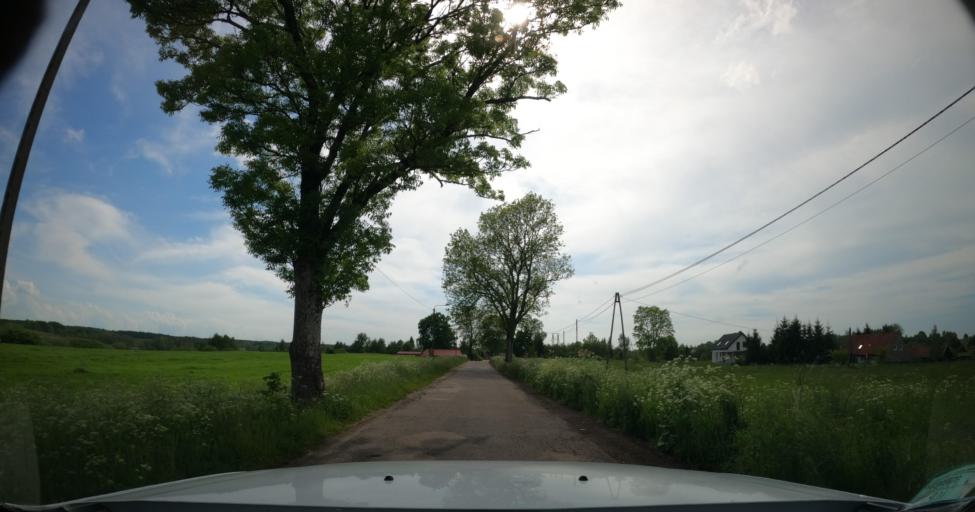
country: PL
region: Warmian-Masurian Voivodeship
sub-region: Powiat lidzbarski
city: Lidzbark Warminski
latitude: 54.1007
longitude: 20.4556
